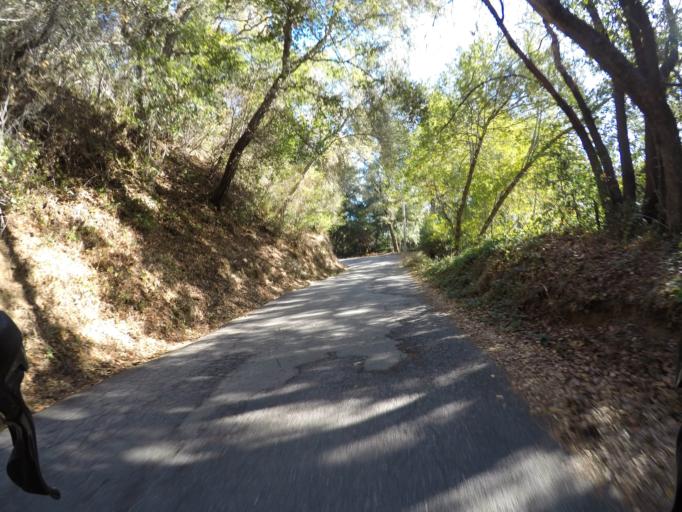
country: US
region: California
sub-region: Santa Cruz County
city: Scotts Valley
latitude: 37.0997
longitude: -121.9938
